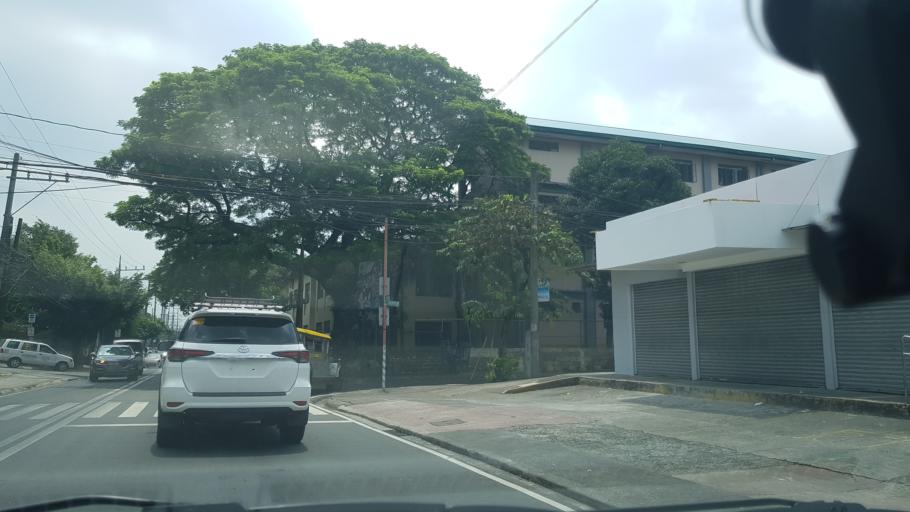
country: PH
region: Calabarzon
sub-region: Province of Rizal
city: Antipolo
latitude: 14.6408
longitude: 121.1220
